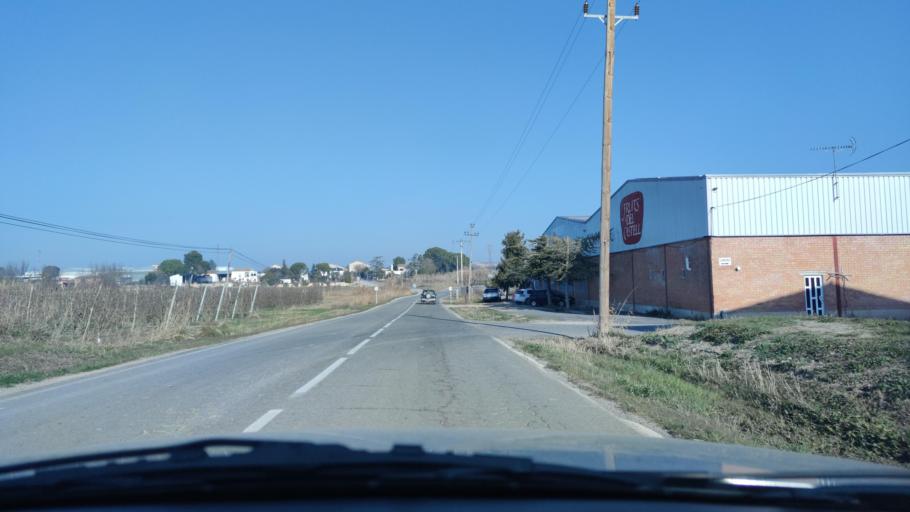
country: ES
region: Catalonia
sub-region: Provincia de Lleida
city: Aspa
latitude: 41.5489
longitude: 0.7347
